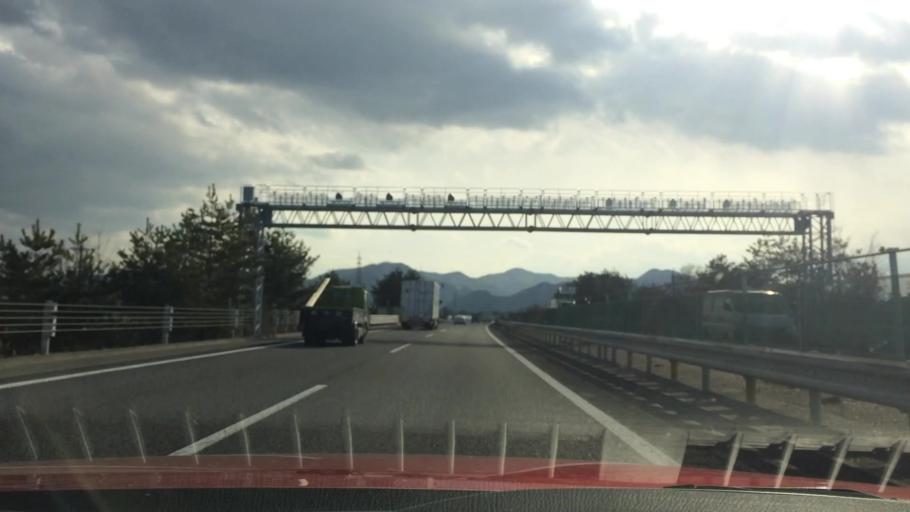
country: JP
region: Nagano
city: Shiojiri
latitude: 36.1486
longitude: 137.9682
